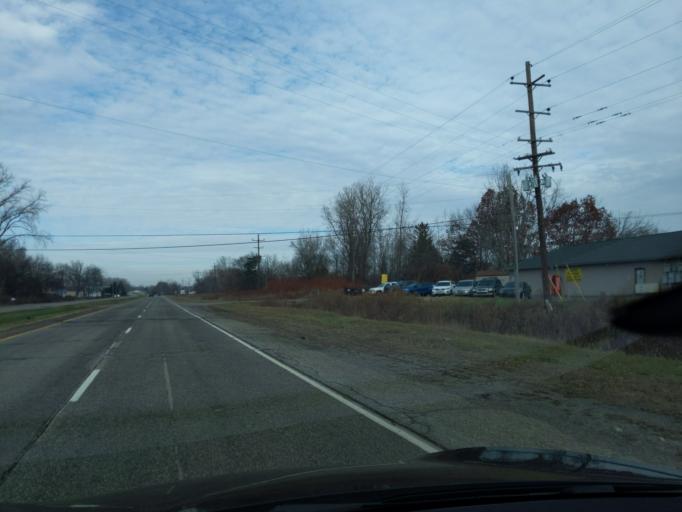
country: US
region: Michigan
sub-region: Ingham County
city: Holt
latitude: 42.6228
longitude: -84.5007
